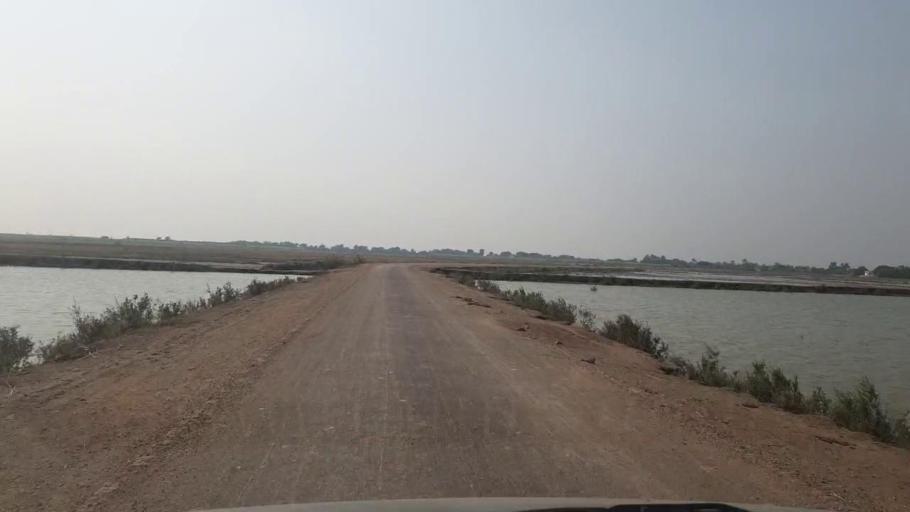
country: PK
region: Sindh
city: Tando Muhammad Khan
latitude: 25.0326
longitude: 68.3893
